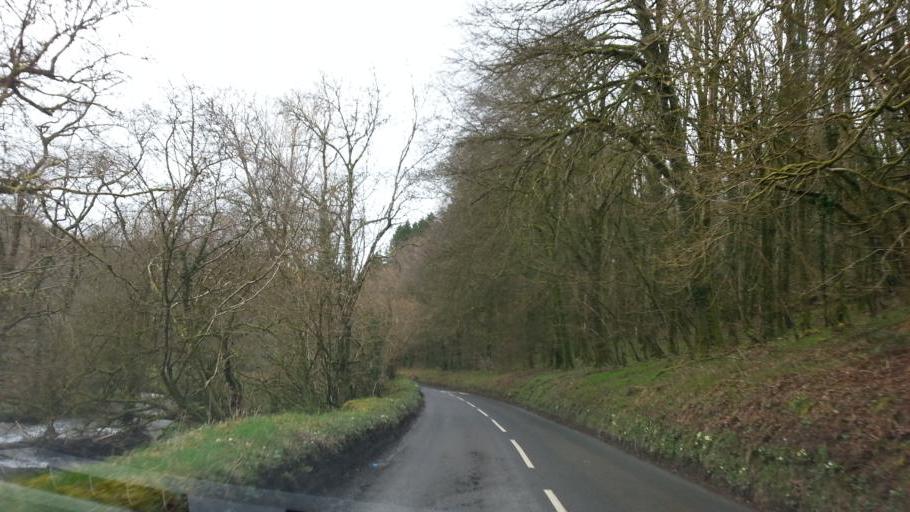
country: GB
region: England
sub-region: Devon
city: Combe Martin
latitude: 51.1494
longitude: -3.9982
